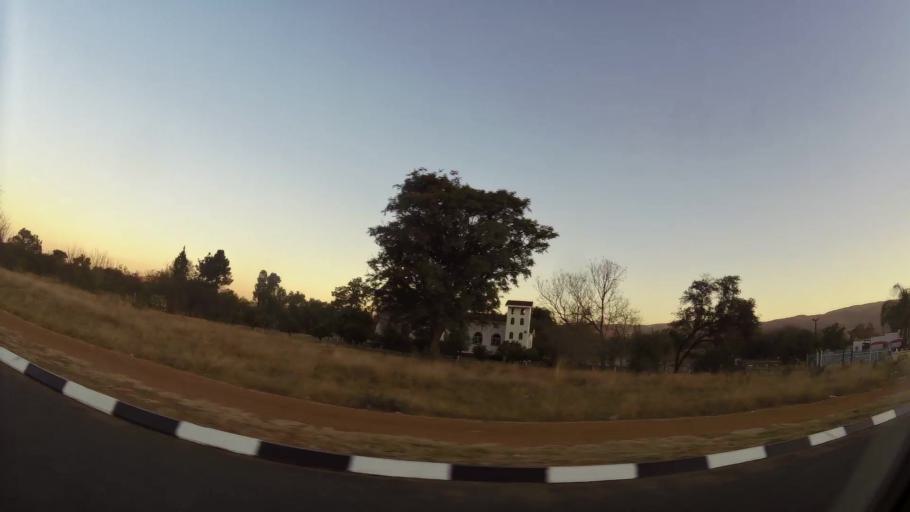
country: ZA
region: North-West
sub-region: Bojanala Platinum District Municipality
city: Rustenburg
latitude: -25.6708
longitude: 27.2192
